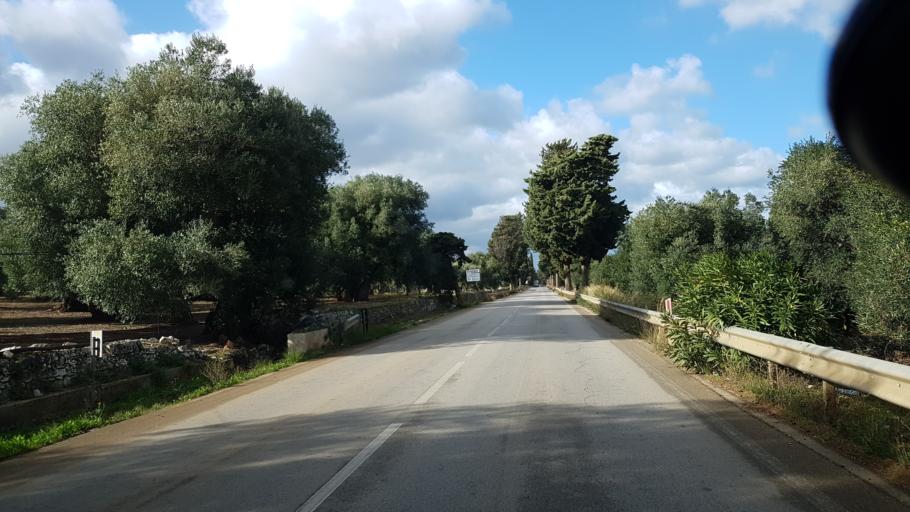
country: IT
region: Apulia
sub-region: Provincia di Brindisi
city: Ostuni
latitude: 40.7507
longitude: 17.5507
